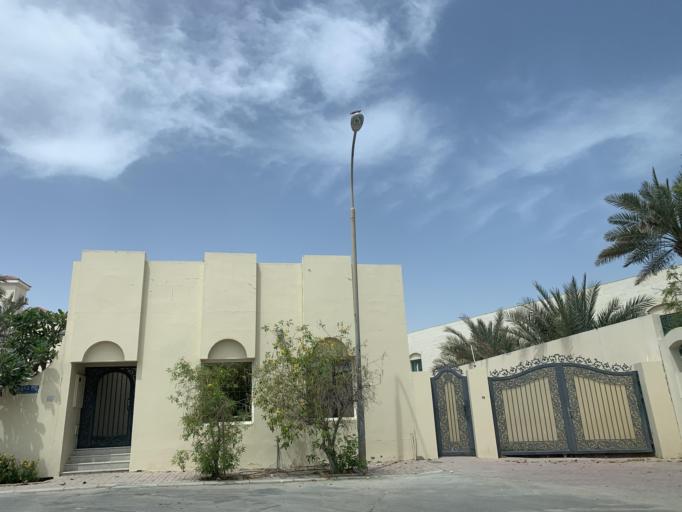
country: BH
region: Northern
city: Ar Rifa'
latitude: 26.1459
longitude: 50.5554
